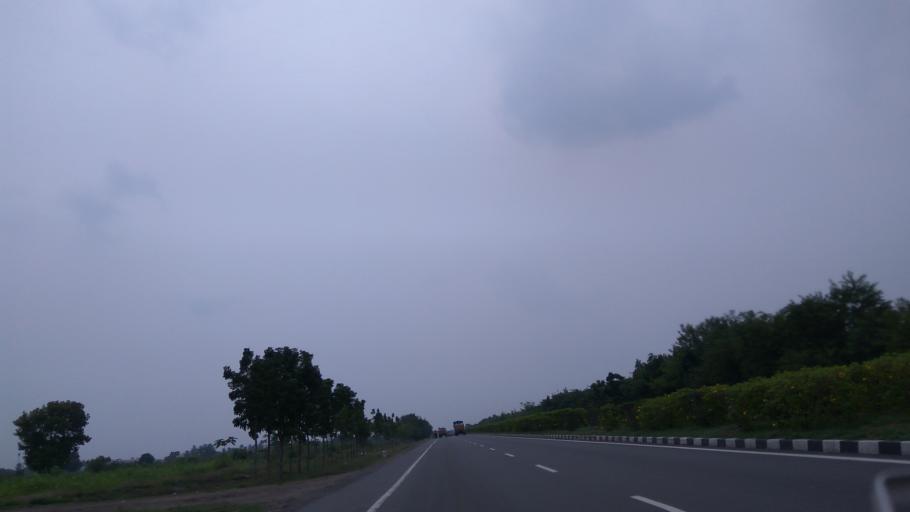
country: IN
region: Tamil Nadu
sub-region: Dharmapuri
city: Dharmapuri
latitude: 12.1235
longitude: 78.1342
